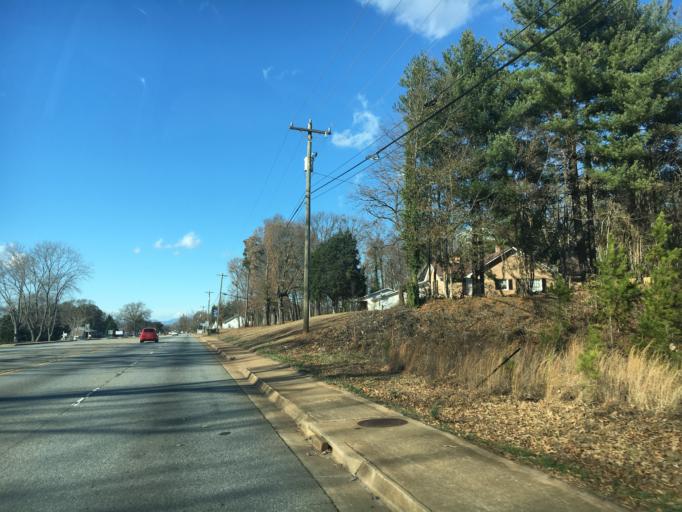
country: US
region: South Carolina
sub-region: Spartanburg County
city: Lyman
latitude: 34.9237
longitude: -82.1183
